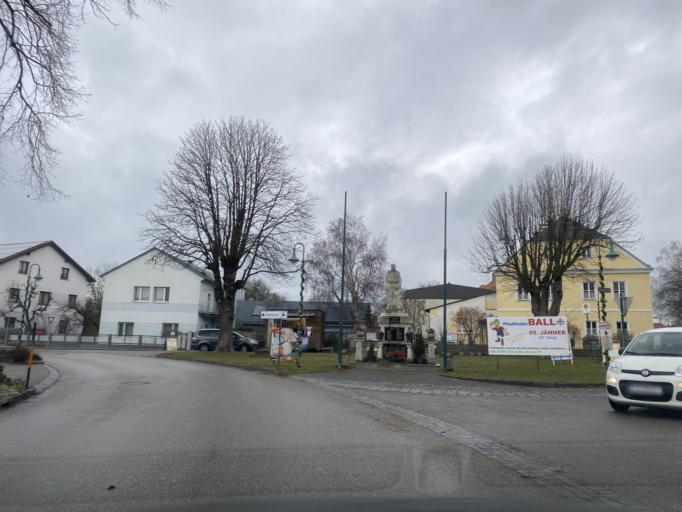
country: AT
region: Lower Austria
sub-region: Politischer Bezirk Sankt Polten
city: Prinzersdorf
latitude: 48.1928
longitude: 15.5013
